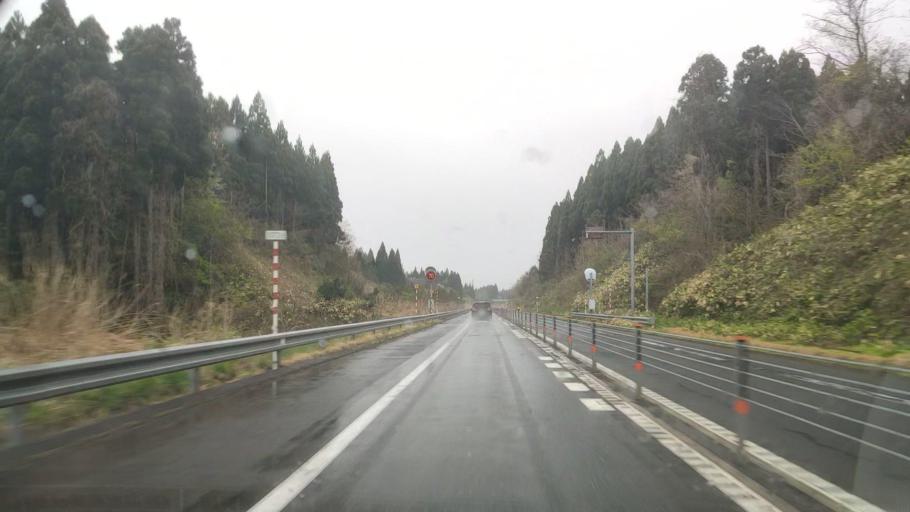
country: JP
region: Akita
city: Noshiromachi
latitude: 40.1732
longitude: 140.0545
